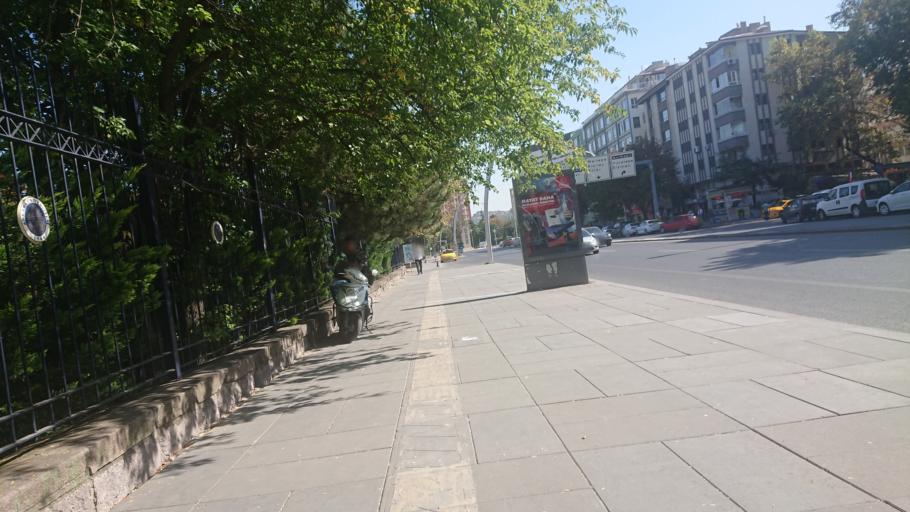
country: TR
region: Ankara
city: Ankara
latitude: 39.9344
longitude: 32.8350
